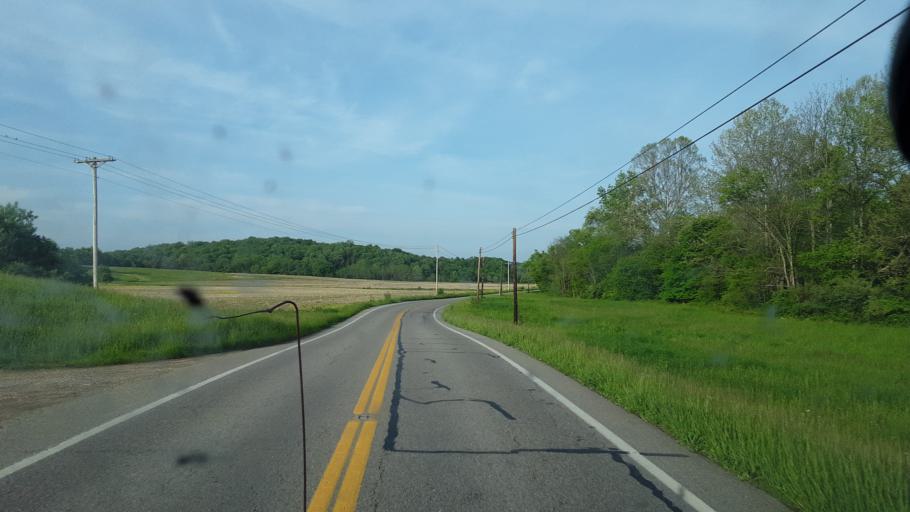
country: US
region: Ohio
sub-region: Ross County
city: Kingston
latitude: 39.4957
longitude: -82.7150
